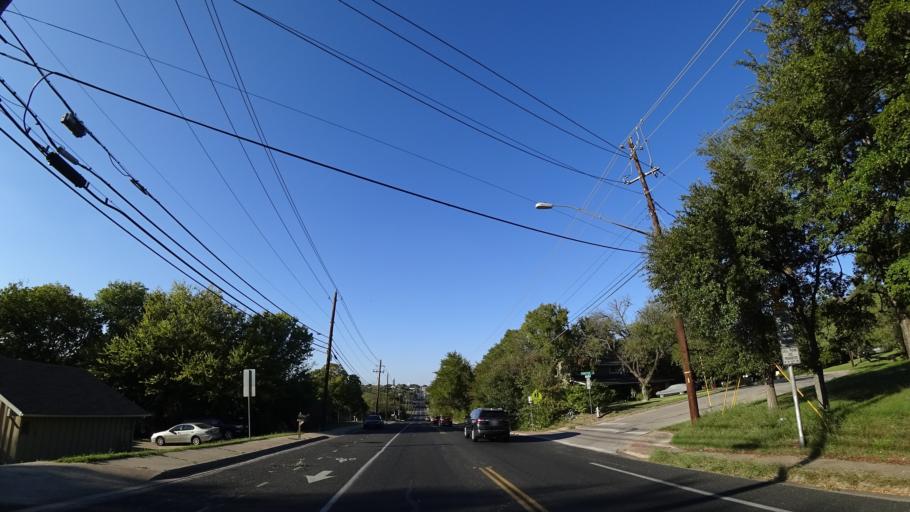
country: US
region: Texas
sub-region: Travis County
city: Austin
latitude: 30.2234
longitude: -97.7347
